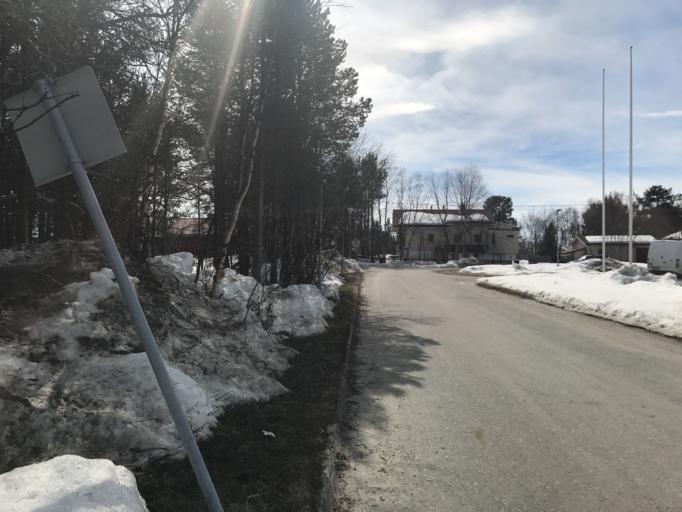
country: NO
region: Finnmark Fylke
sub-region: Karasjok
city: Karasjohka
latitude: 69.4748
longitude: 25.5164
